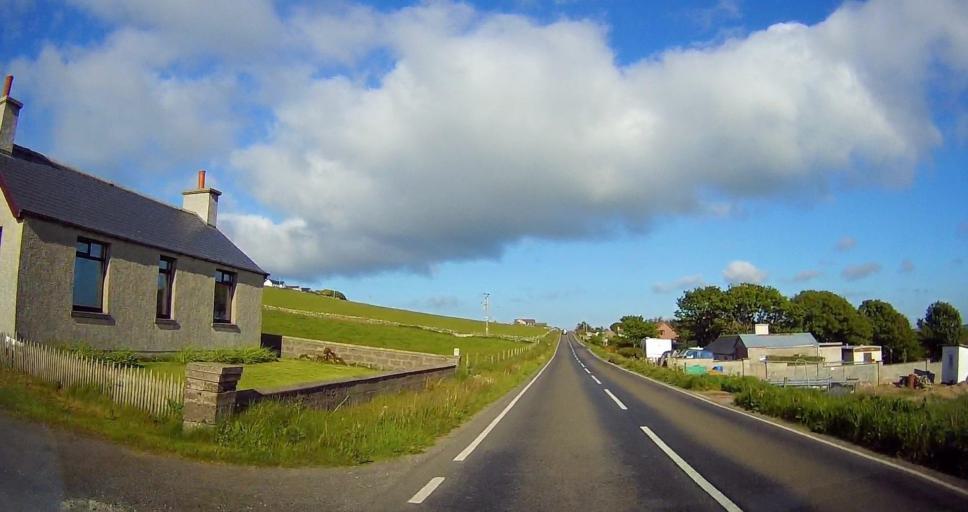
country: GB
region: Scotland
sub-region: Orkney Islands
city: Orkney
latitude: 58.9787
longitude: -3.0205
